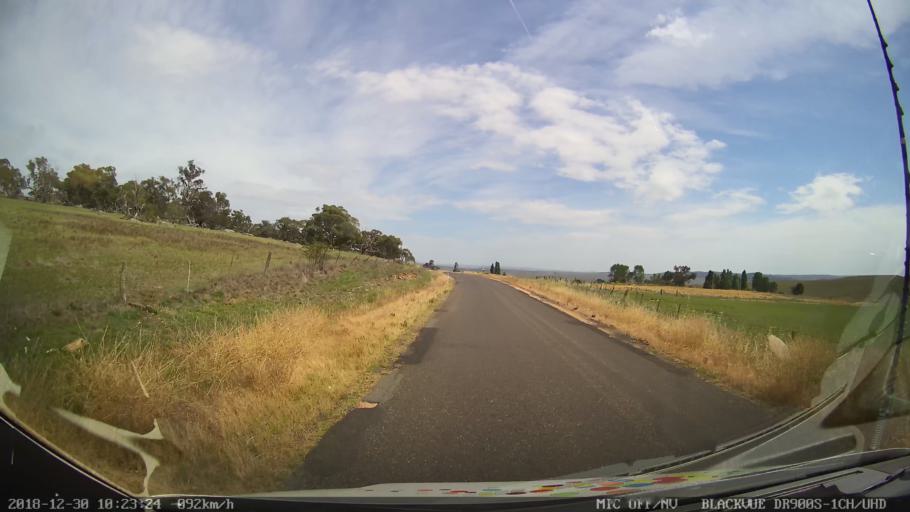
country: AU
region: New South Wales
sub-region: Snowy River
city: Berridale
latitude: -36.5380
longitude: 148.9824
